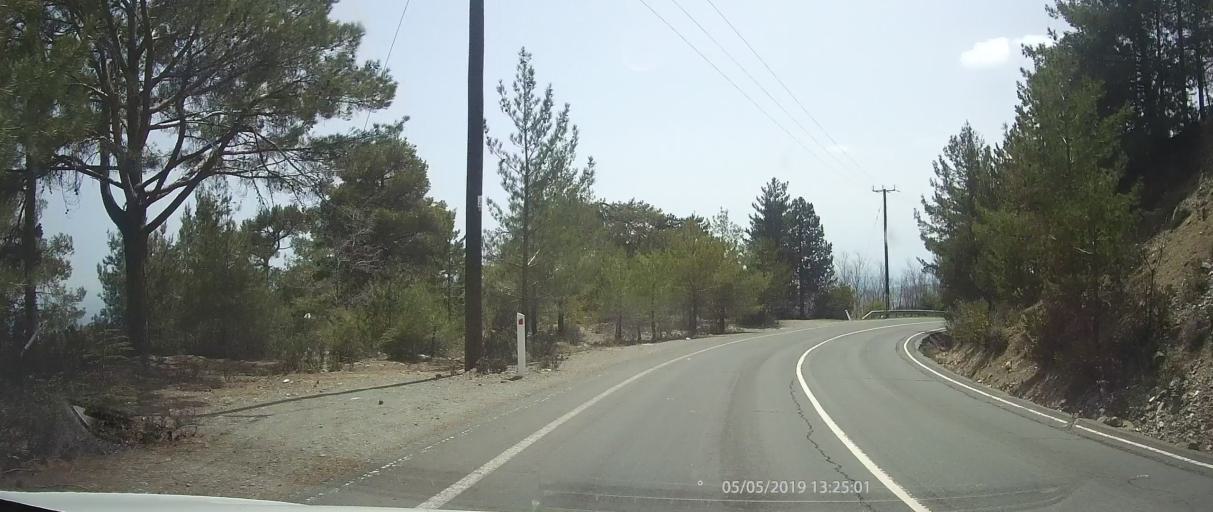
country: CY
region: Lefkosia
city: Kakopetria
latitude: 34.9083
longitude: 32.8662
